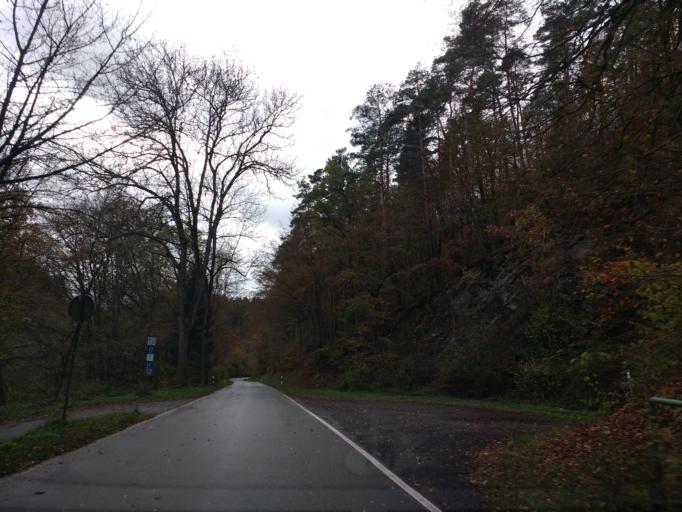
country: DE
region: Hesse
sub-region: Regierungsbezirk Kassel
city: Vohl
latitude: 51.1915
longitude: 8.9498
